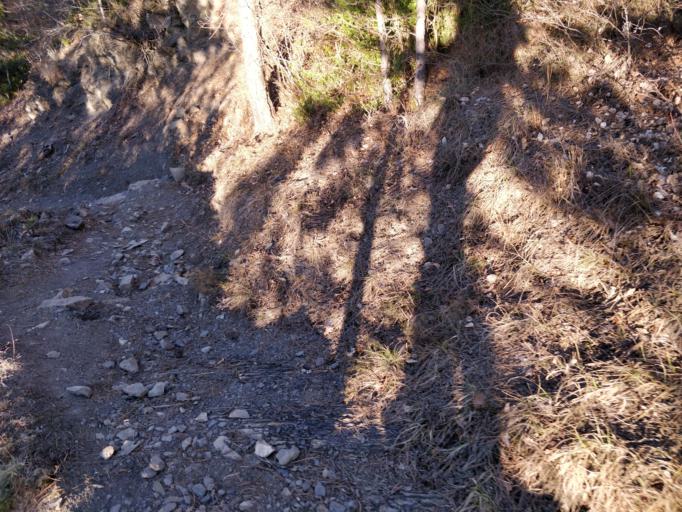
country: FR
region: Provence-Alpes-Cote d'Azur
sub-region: Departement des Alpes-de-Haute-Provence
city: Digne-les-Bains
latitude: 44.0992
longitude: 6.2523
